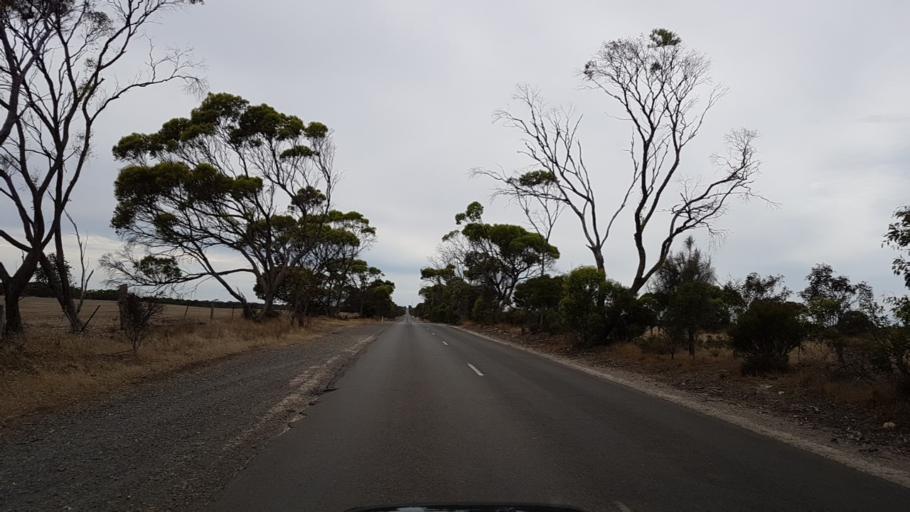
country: AU
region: South Australia
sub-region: Yorke Peninsula
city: Honiton
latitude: -34.9850
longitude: 137.2246
